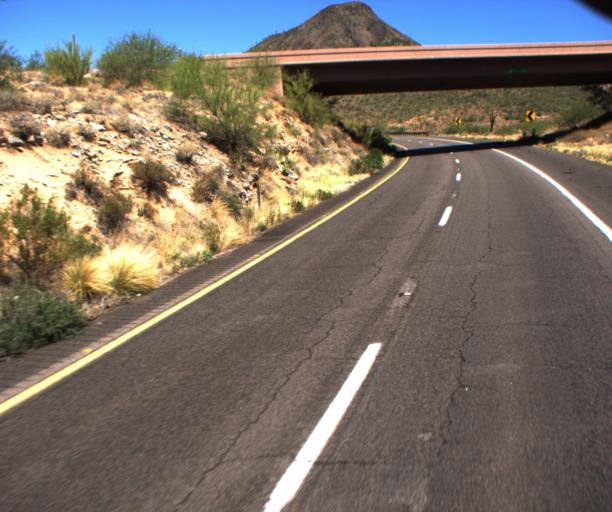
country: US
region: Arizona
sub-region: Gila County
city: Tonto Basin
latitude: 33.8056
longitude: -111.4864
